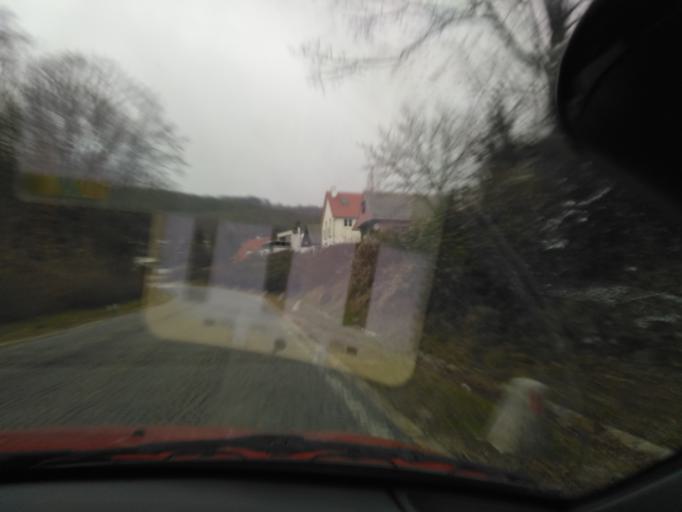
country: AT
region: Lower Austria
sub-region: Politischer Bezirk Wien-Umgebung
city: Klosterneuburg
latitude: 48.2514
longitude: 16.2786
